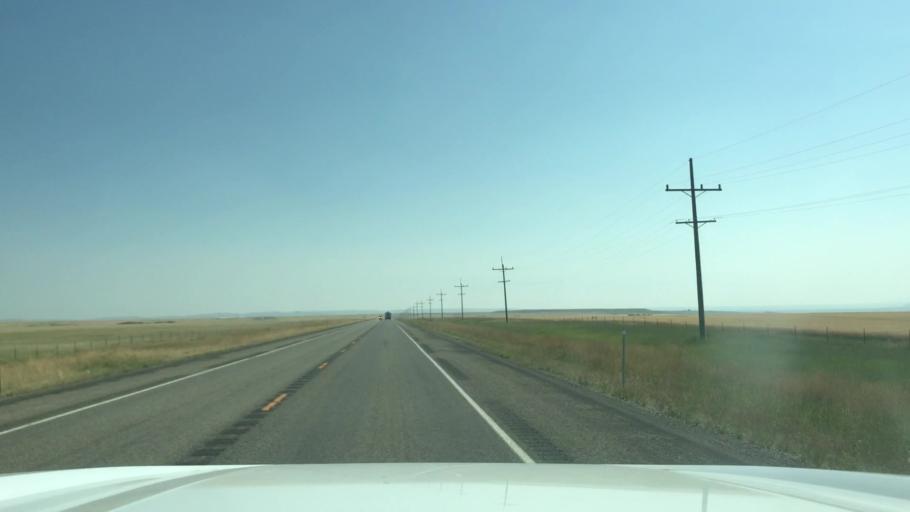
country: US
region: Montana
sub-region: Wheatland County
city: Harlowton
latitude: 46.5083
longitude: -109.7659
